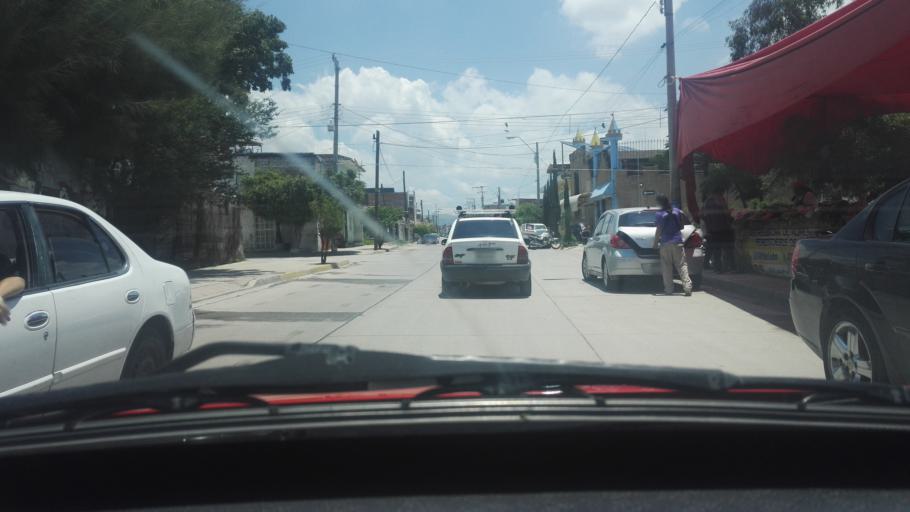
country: MX
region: Guanajuato
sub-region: Leon
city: San Jose de Duran (Los Troncoso)
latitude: 21.0811
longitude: -101.6348
